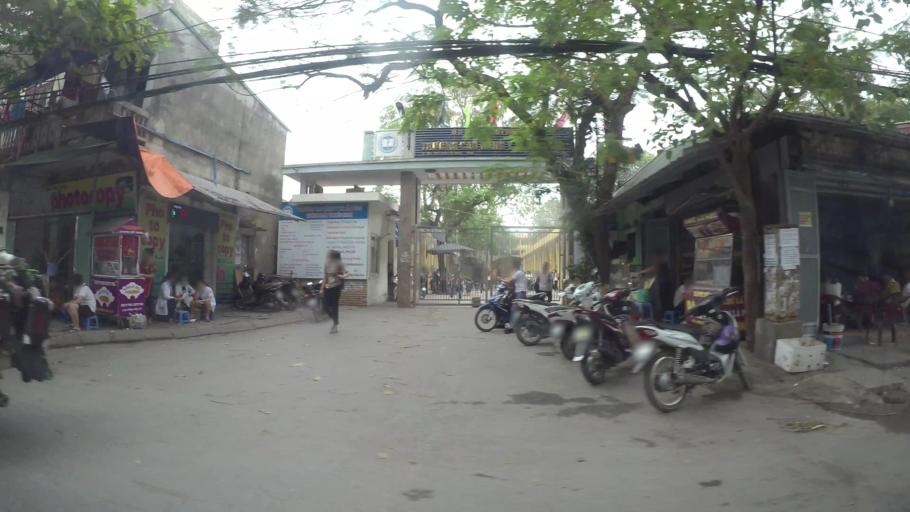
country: VN
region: Ha Noi
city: Ha Dong
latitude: 20.9709
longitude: 105.7732
